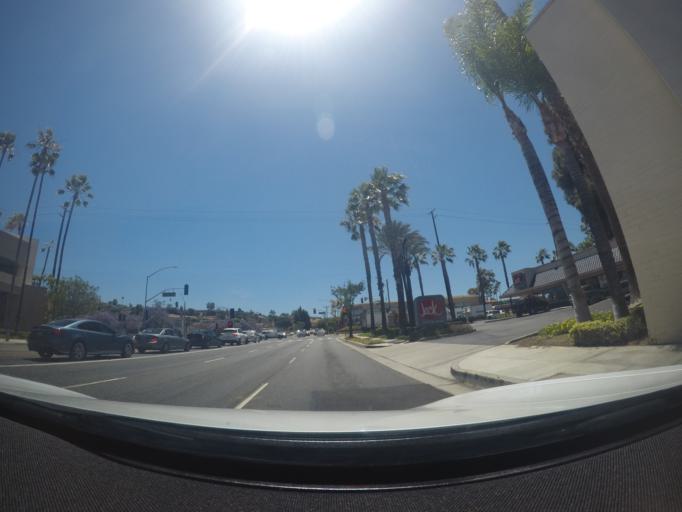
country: US
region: California
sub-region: Los Angeles County
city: Lomita
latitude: 33.7925
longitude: -118.3328
